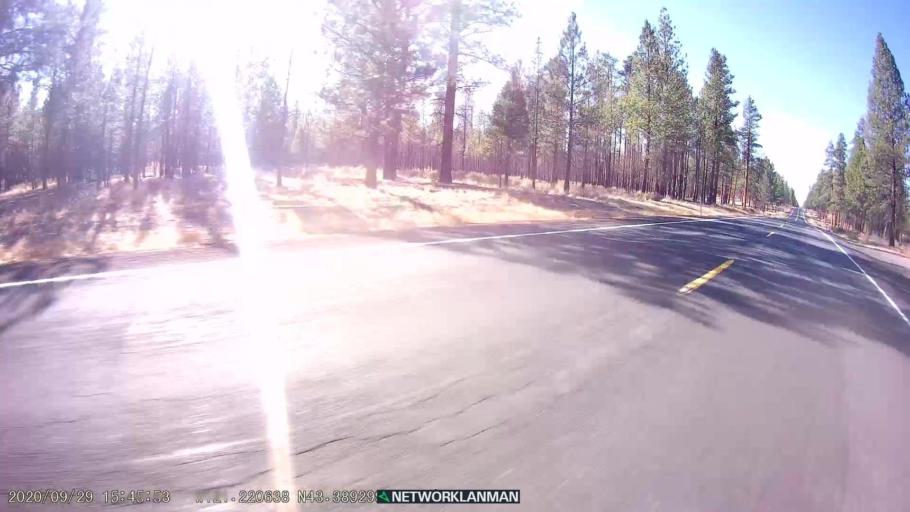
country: US
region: Oregon
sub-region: Deschutes County
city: La Pine
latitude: 43.3894
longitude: -121.2207
